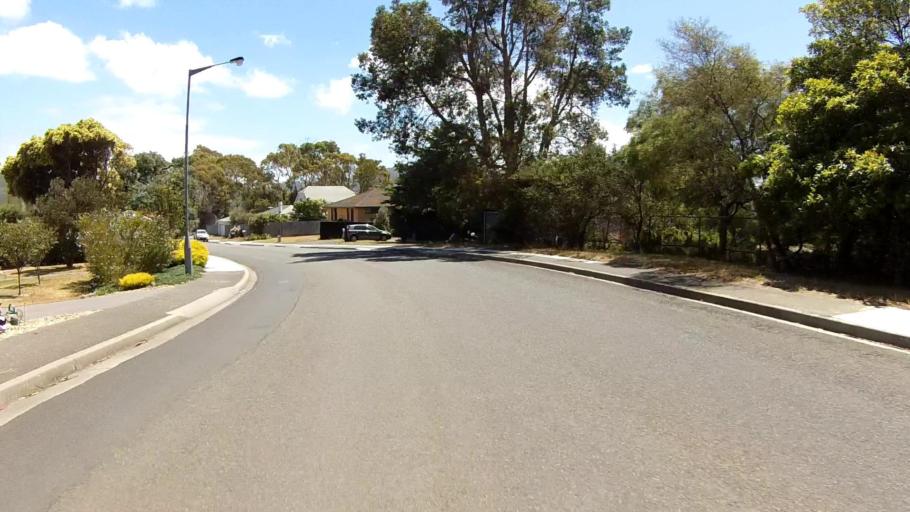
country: AU
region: Tasmania
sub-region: Clarence
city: Sandford
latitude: -42.9182
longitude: 147.5042
